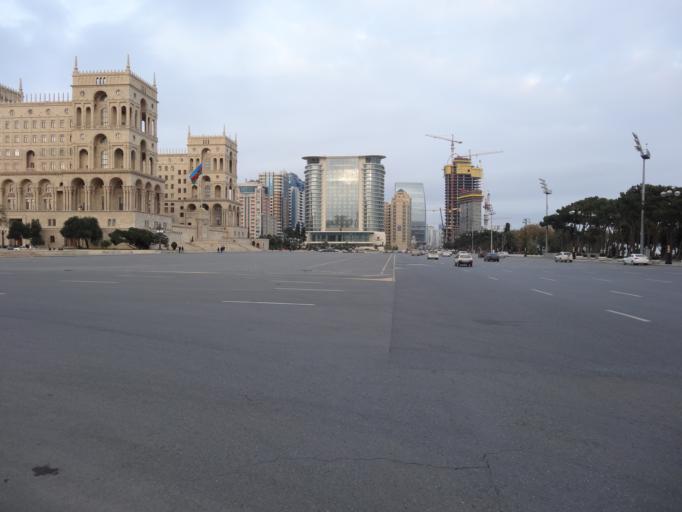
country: AZ
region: Baki
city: Baku
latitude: 40.3720
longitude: 49.8509
